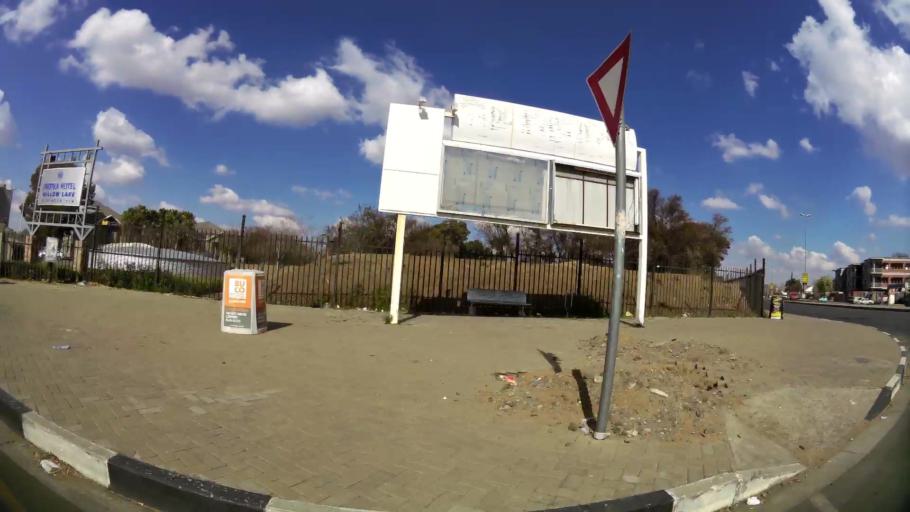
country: ZA
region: Orange Free State
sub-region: Mangaung Metropolitan Municipality
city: Bloemfontein
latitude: -29.1118
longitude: 26.2018
